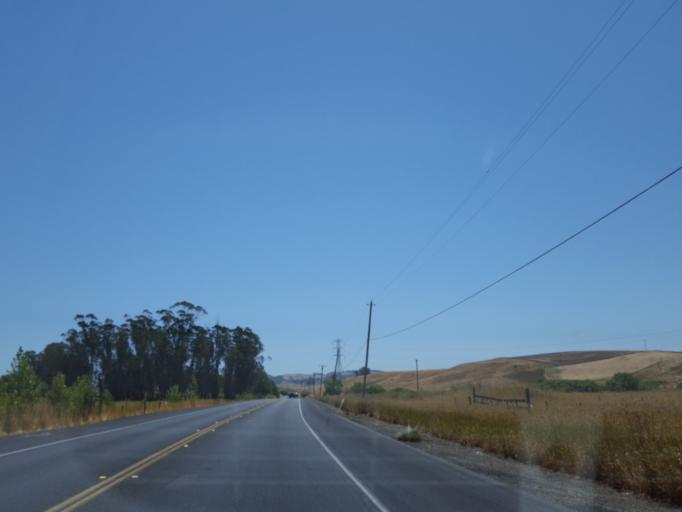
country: US
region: California
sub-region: Sonoma County
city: Petaluma
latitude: 38.2530
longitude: -122.5667
